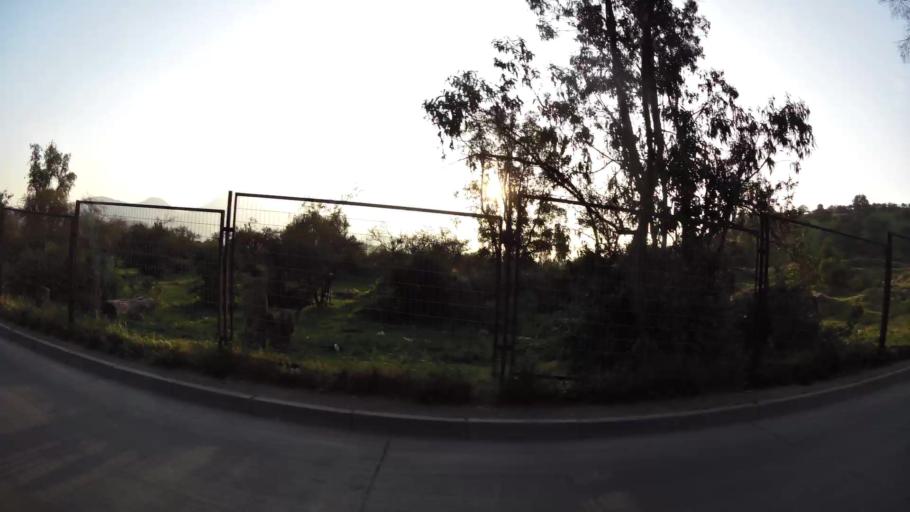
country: CL
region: Santiago Metropolitan
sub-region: Provincia de Chacabuco
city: Chicureo Abajo
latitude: -33.3271
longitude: -70.5194
